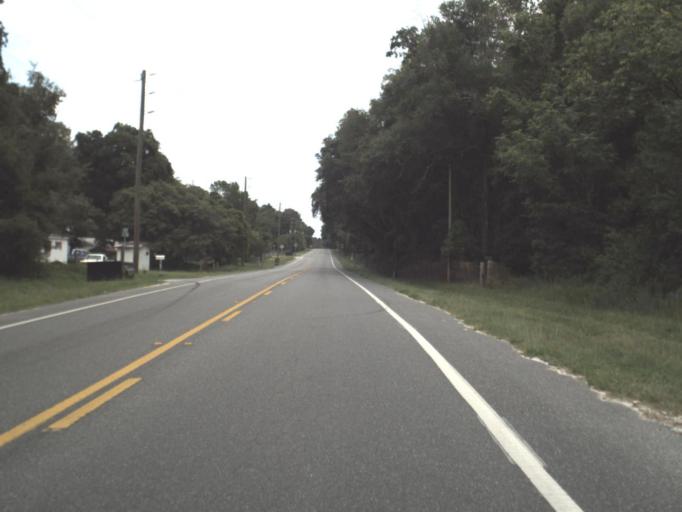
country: US
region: Florida
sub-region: Pasco County
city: Lacoochee
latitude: 28.4675
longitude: -82.1679
